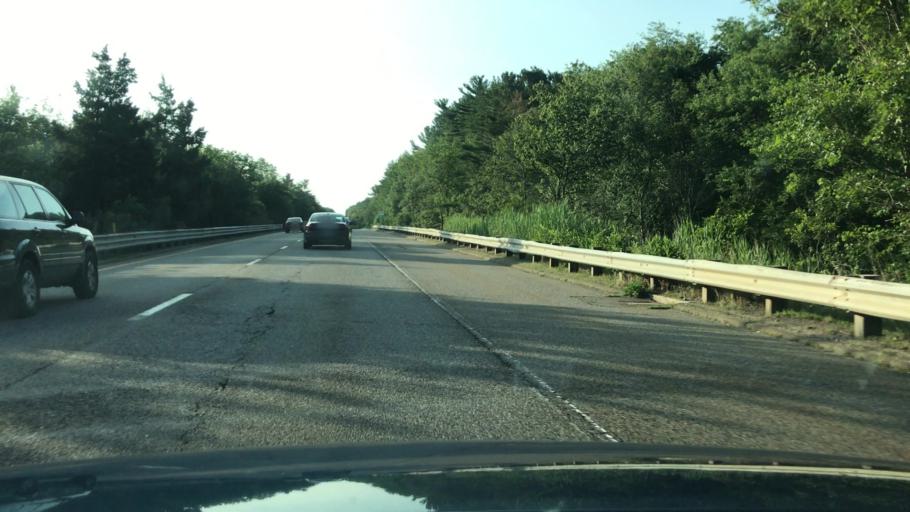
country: US
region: Massachusetts
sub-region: Plymouth County
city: Hanover
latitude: 42.1398
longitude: -70.8242
